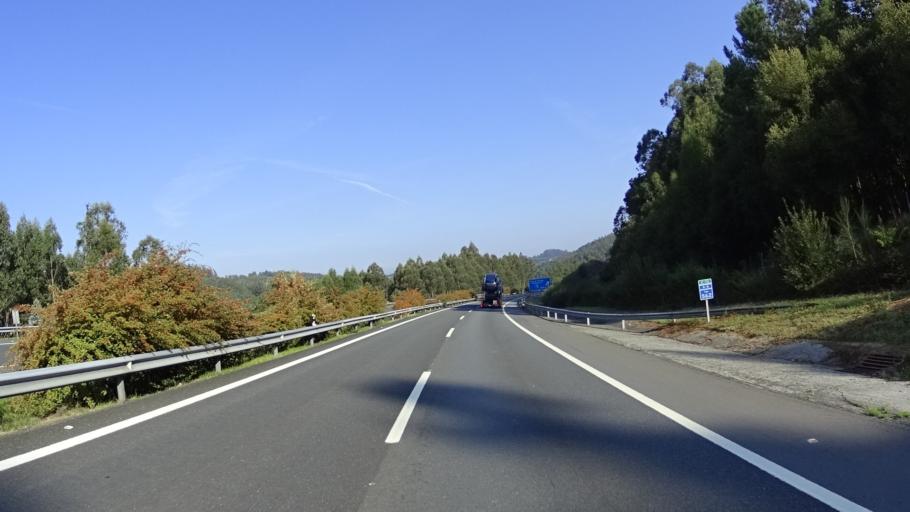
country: ES
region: Galicia
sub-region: Provincia da Coruna
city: Coiros
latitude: 43.2476
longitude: -8.1789
